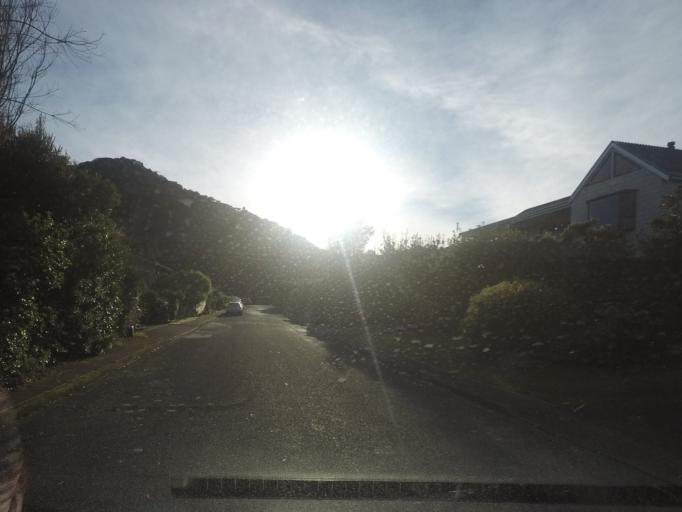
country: NZ
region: Tasman
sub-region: Tasman District
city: Takaka
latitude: -40.8105
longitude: 172.9165
